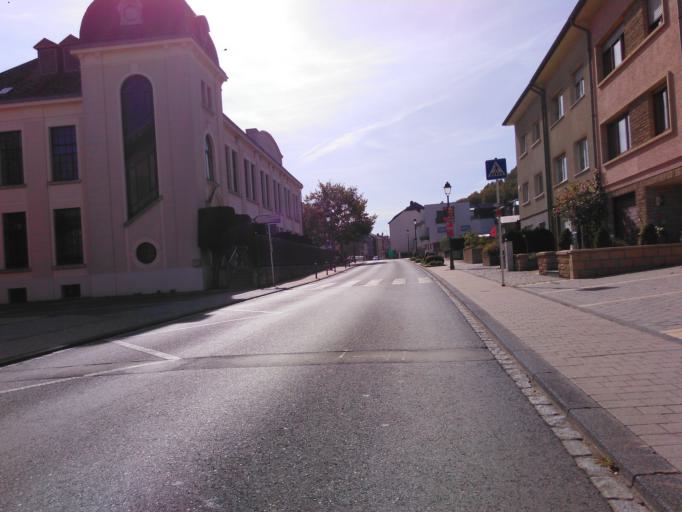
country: LU
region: Luxembourg
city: Tetange
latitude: 49.4775
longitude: 6.0358
